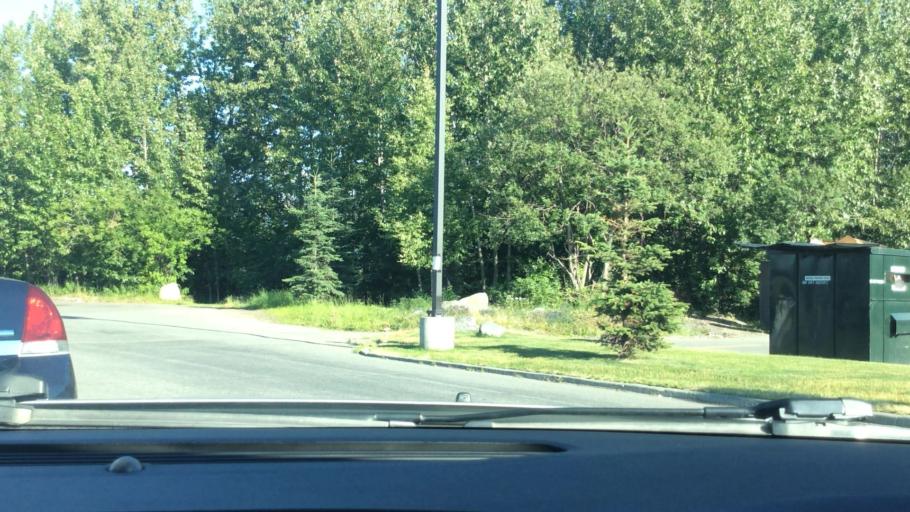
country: US
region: Alaska
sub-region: Anchorage Municipality
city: Anchorage
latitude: 61.2089
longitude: -149.7752
